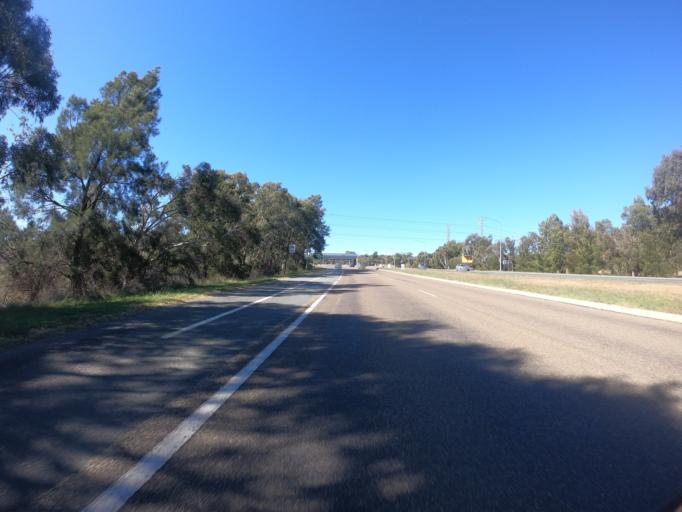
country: AU
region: Australian Capital Territory
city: Kaleen
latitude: -35.2423
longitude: 149.1080
